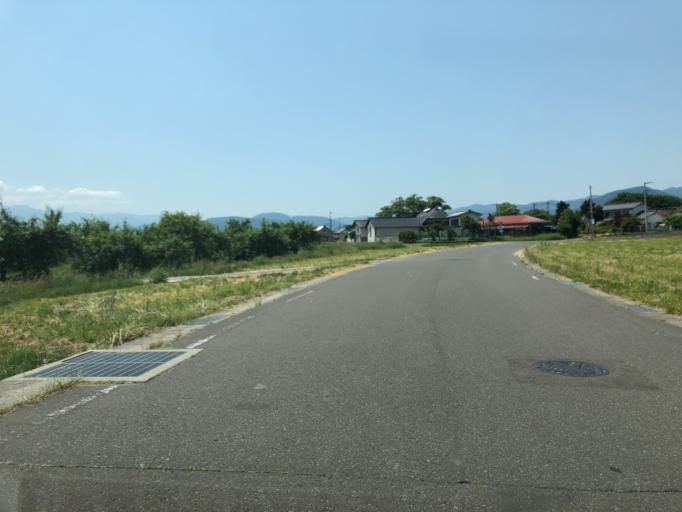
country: JP
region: Fukushima
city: Hobaramachi
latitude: 37.8195
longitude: 140.4820
